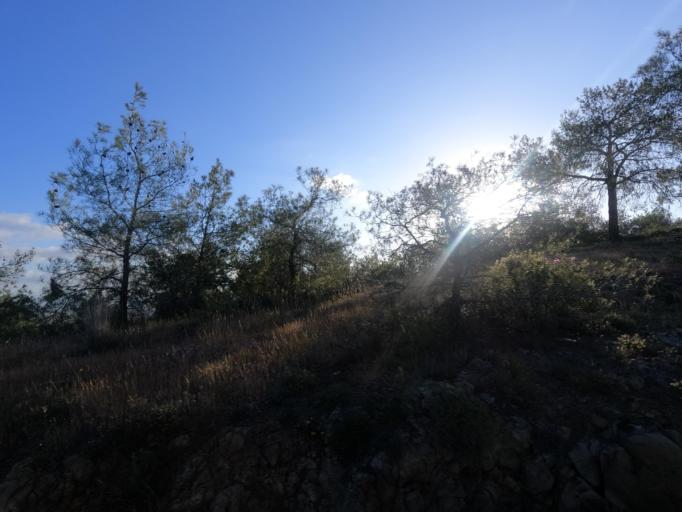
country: CY
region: Lefkosia
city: Peristerona
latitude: 35.0648
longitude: 33.0397
